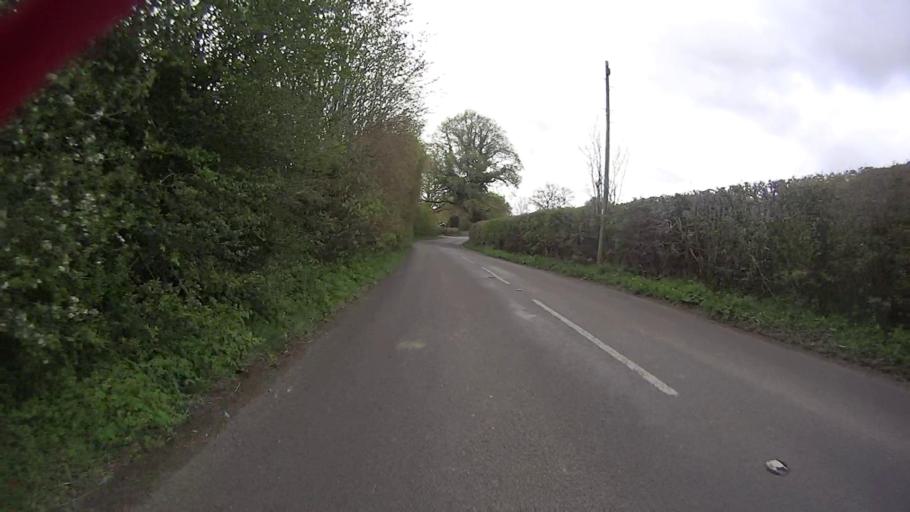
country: GB
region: England
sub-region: Surrey
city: Newdigate
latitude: 51.1289
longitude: -0.2783
